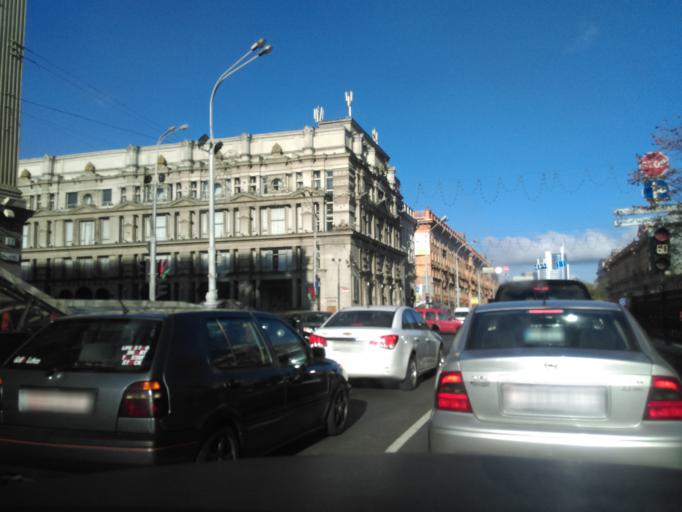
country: BY
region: Minsk
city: Minsk
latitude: 53.9004
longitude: 27.5592
